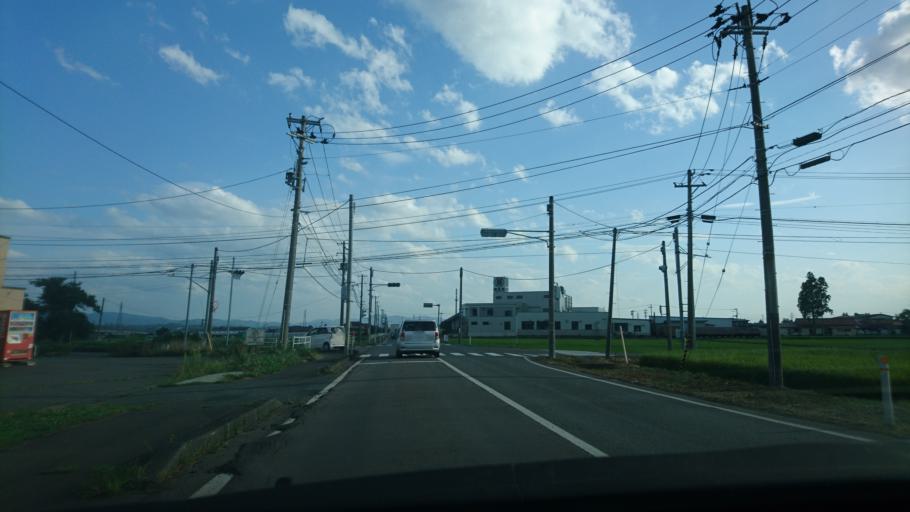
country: JP
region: Iwate
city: Mizusawa
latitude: 39.1647
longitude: 141.1804
